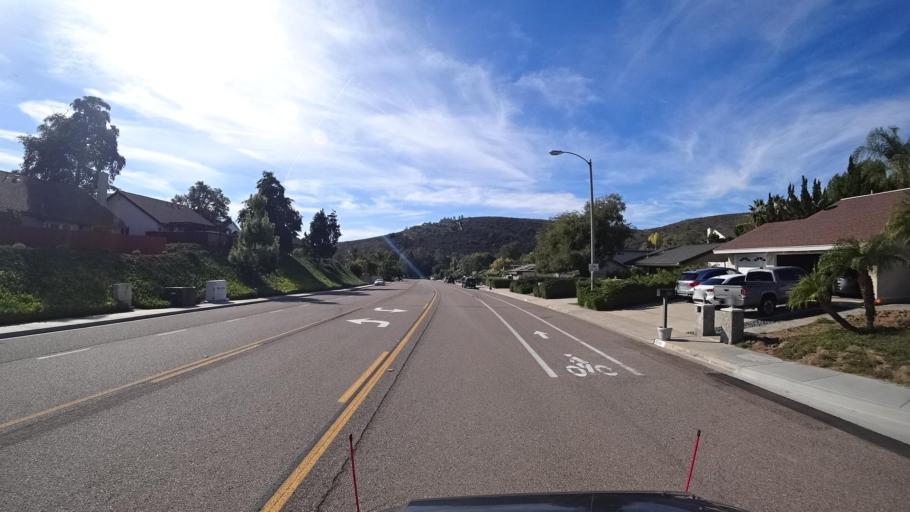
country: US
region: California
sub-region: San Diego County
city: Spring Valley
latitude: 32.7294
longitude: -116.9834
